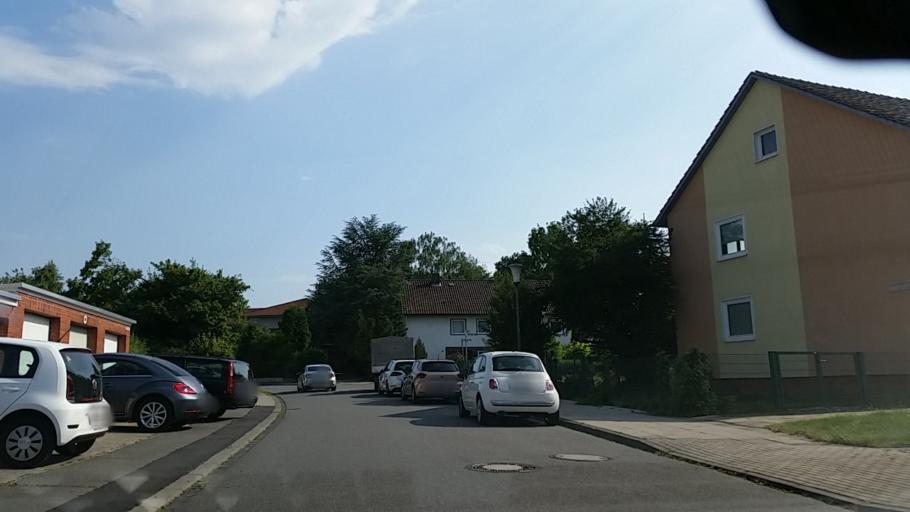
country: DE
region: Lower Saxony
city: Wolfsburg
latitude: 52.4090
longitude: 10.7490
